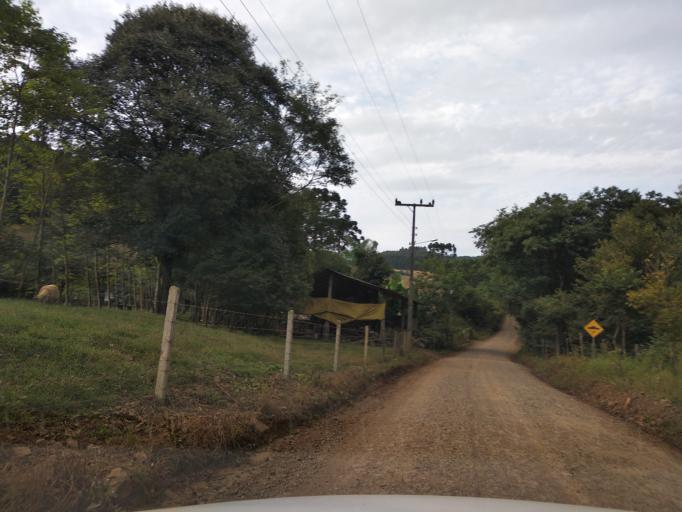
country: BR
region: Santa Catarina
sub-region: Videira
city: Videira
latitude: -26.9560
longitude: -51.1626
